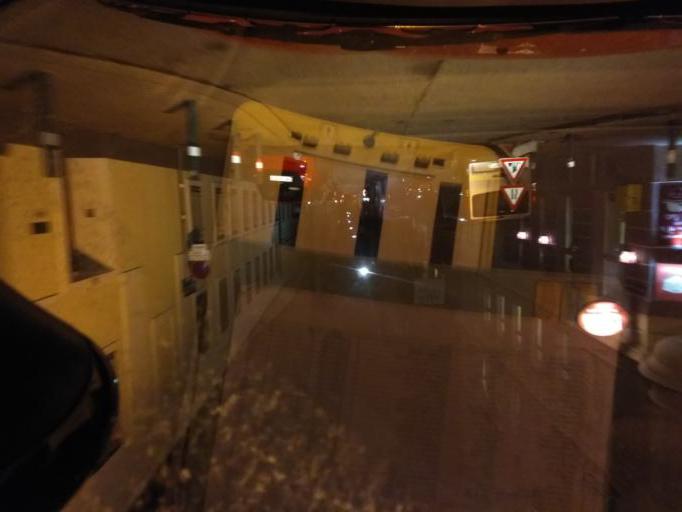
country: AT
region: Vienna
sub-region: Wien Stadt
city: Vienna
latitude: 48.1895
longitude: 16.3591
